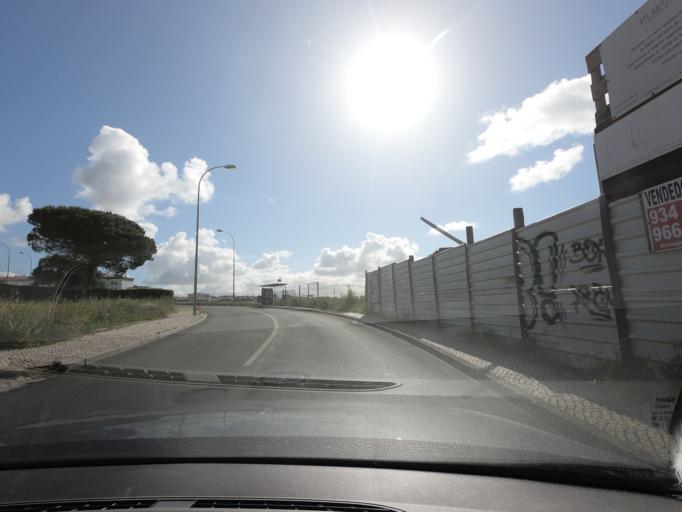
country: PT
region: Lisbon
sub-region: Oeiras
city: Paco de Arcos
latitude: 38.7000
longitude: -9.2983
